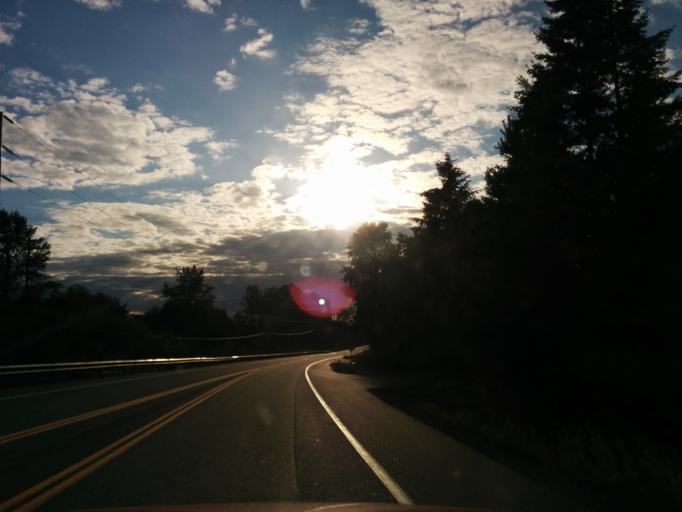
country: US
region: Washington
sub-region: Snohomish County
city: Woods Creek
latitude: 47.8549
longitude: -121.9042
